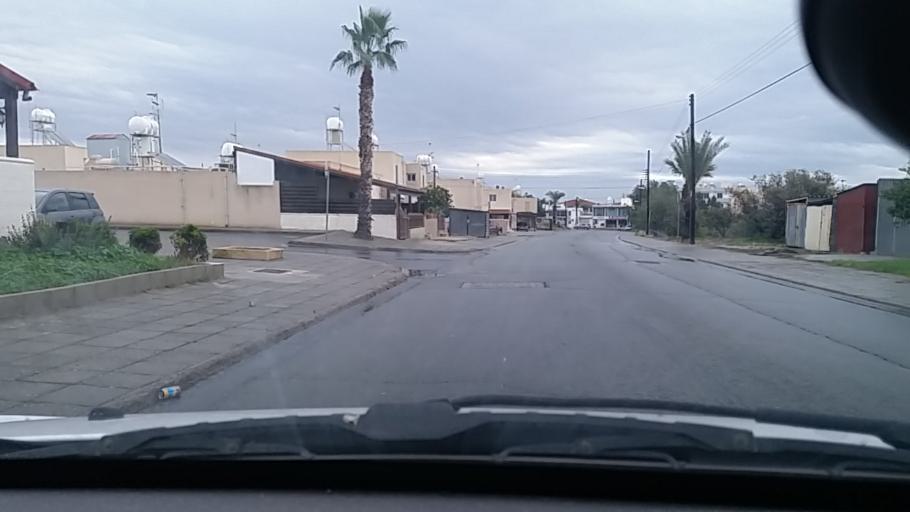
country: CY
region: Larnaka
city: Livadia
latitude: 34.9372
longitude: 33.6238
